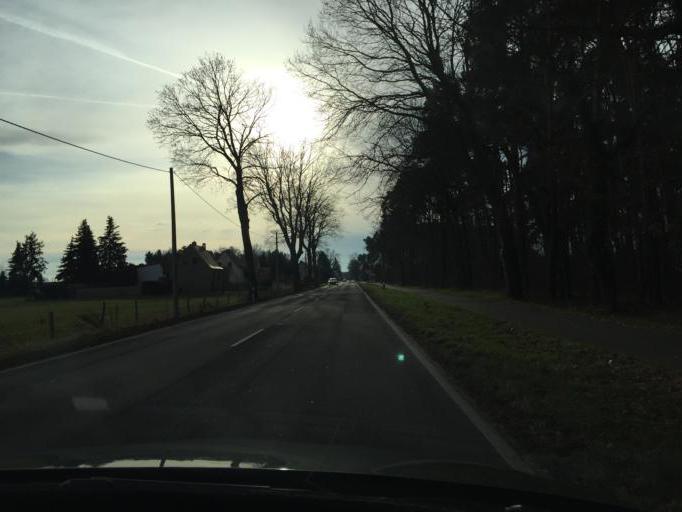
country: DE
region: Brandenburg
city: Peitz
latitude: 51.8737
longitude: 14.4187
